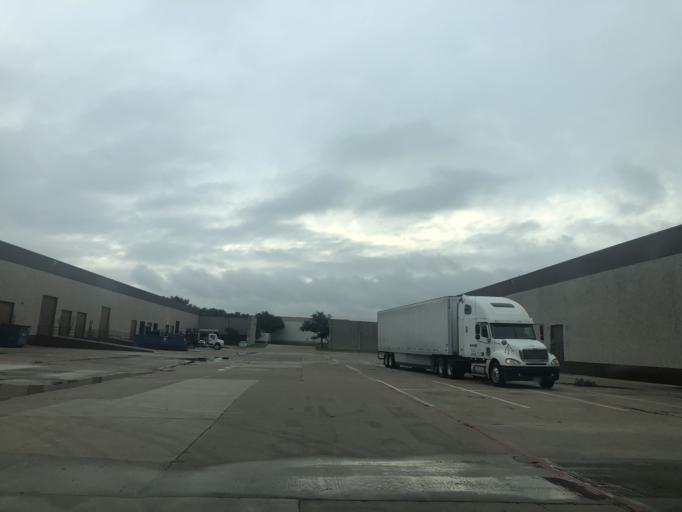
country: US
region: Texas
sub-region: Dallas County
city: Cockrell Hill
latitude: 32.7732
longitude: -96.8812
